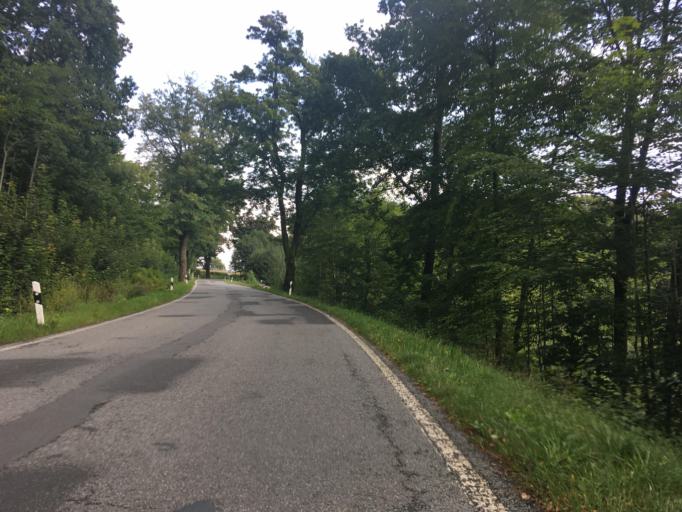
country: CZ
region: Ustecky
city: Mikulasovice
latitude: 50.9241
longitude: 14.3472
